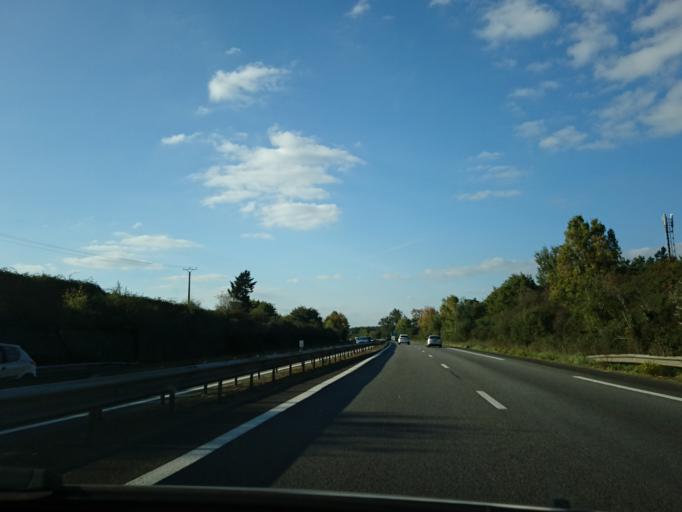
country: FR
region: Pays de la Loire
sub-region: Departement de la Loire-Atlantique
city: Orvault
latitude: 47.2896
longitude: -1.6100
